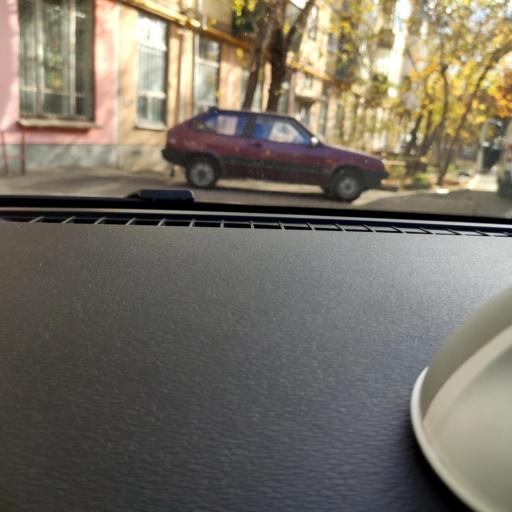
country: RU
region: Samara
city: Samara
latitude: 53.1881
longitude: 50.1872
